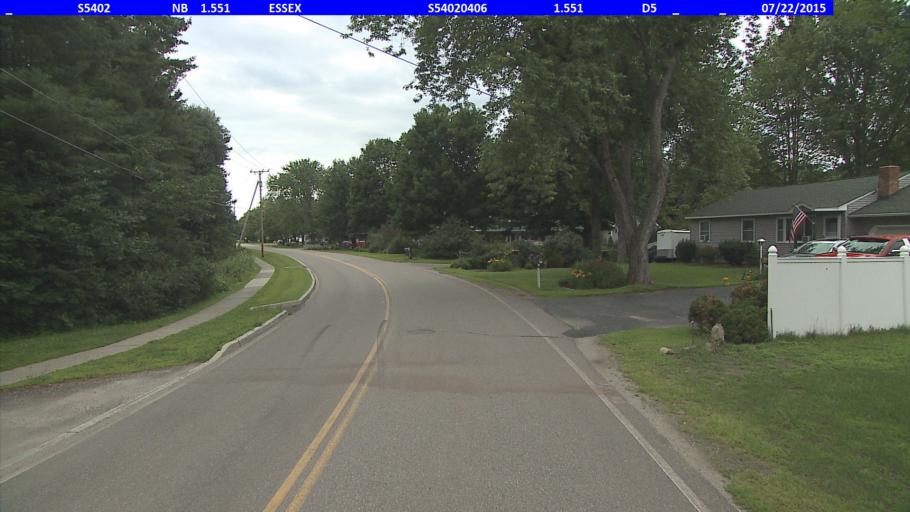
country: US
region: Vermont
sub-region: Chittenden County
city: Jericho
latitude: 44.5004
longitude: -73.0490
